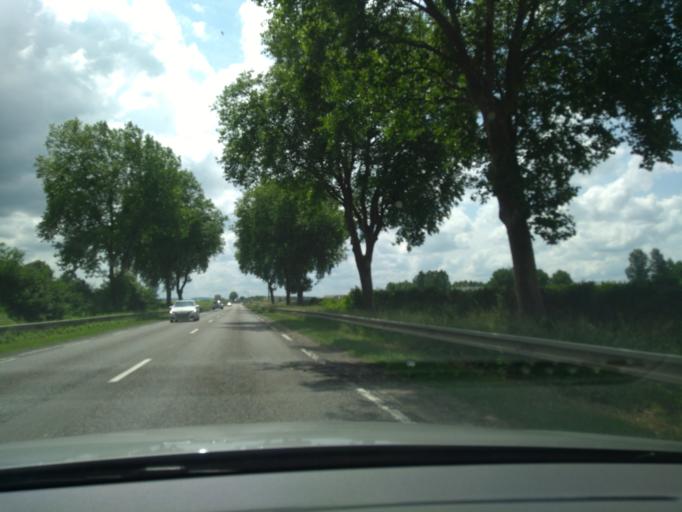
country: FR
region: Picardie
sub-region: Departement de l'Aisne
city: Athies-sous-Laon
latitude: 49.5856
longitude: 3.6584
